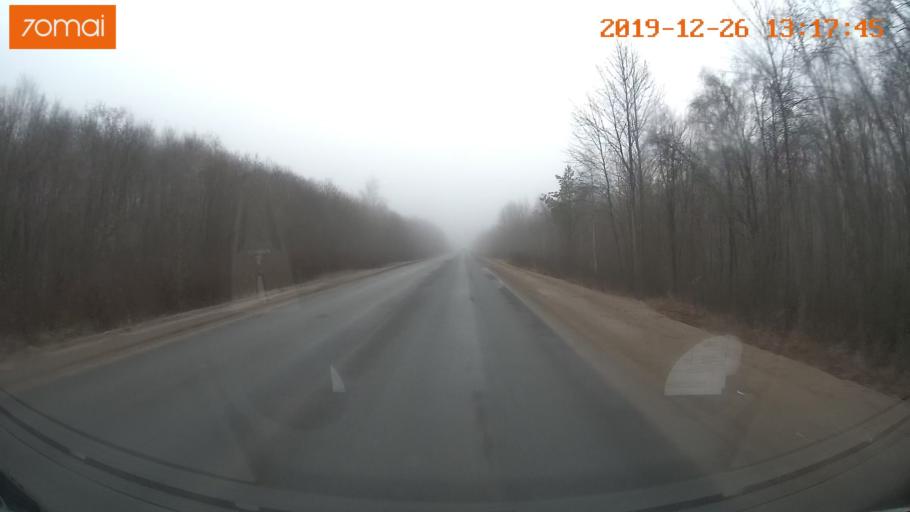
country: RU
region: Vologda
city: Cherepovets
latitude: 58.9655
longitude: 38.1172
